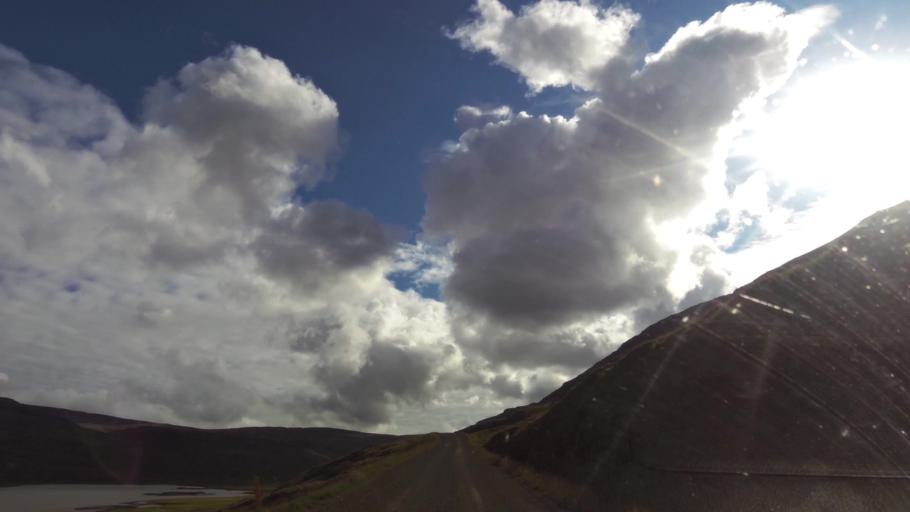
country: IS
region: West
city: Olafsvik
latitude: 65.5698
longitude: -24.1659
